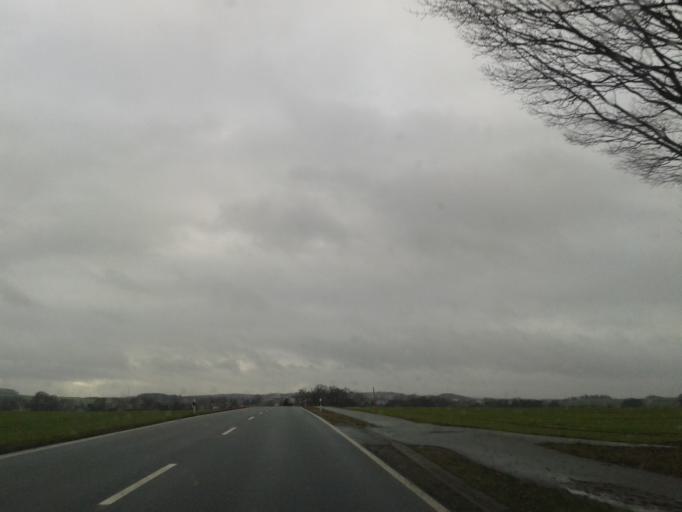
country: DE
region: Saxony
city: Durrhennersdorf
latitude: 51.0145
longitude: 14.6221
